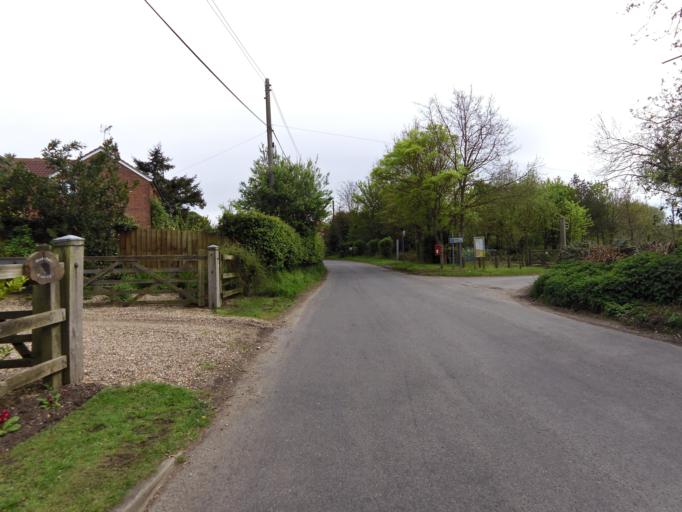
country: GB
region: England
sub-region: Suffolk
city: Ipswich
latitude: 51.9718
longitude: 1.1680
